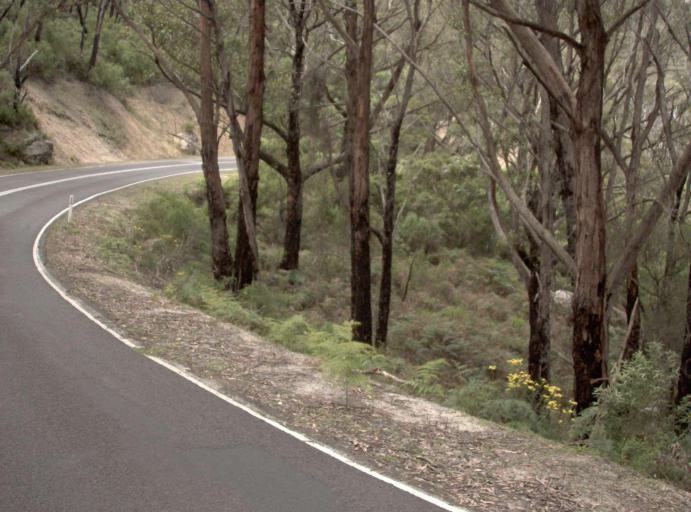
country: AU
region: Victoria
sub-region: Latrobe
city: Morwell
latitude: -39.0167
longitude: 146.3065
